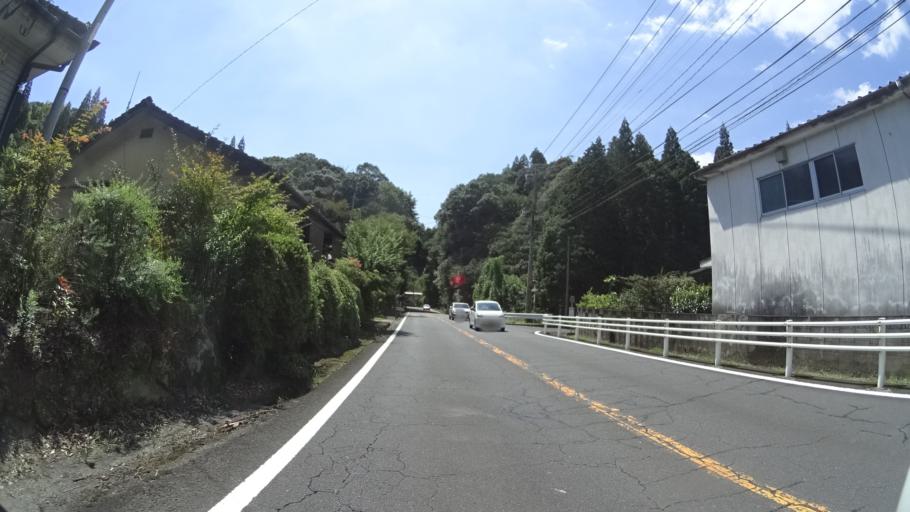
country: JP
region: Kagoshima
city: Kokubu-matsuki
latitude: 31.8418
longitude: 130.7498
